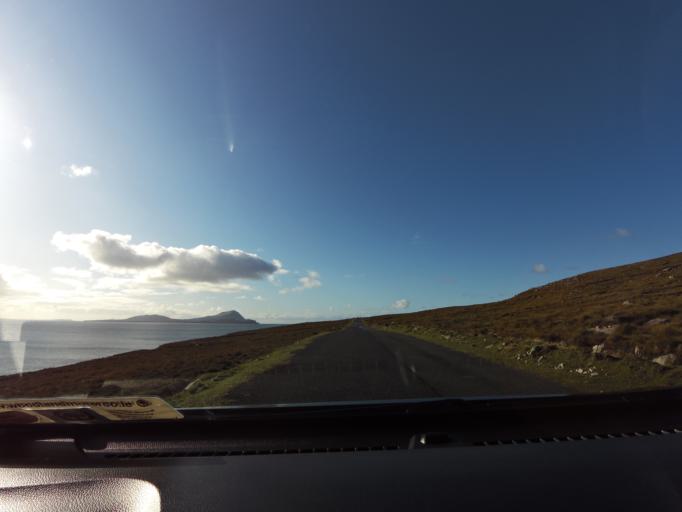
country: IE
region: Connaught
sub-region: Maigh Eo
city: Westport
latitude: 53.8679
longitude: -9.8616
